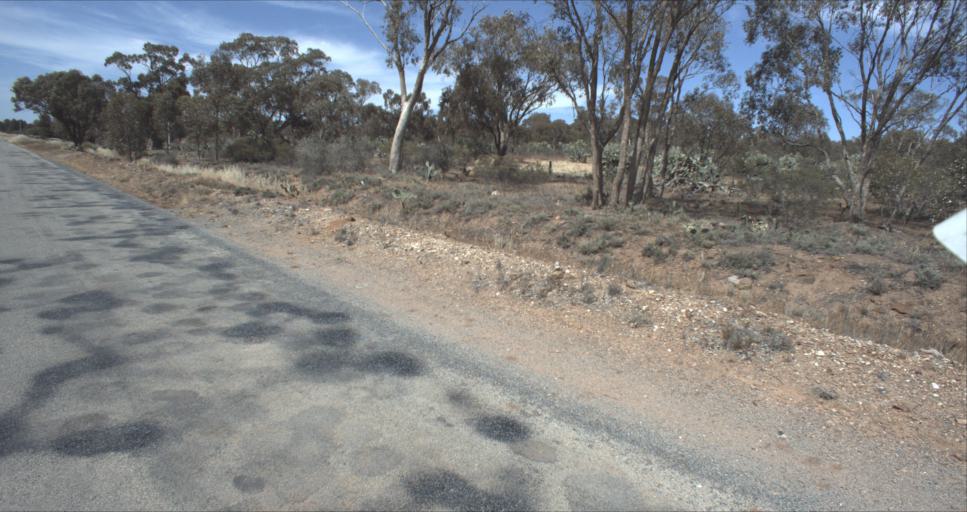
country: AU
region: New South Wales
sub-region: Leeton
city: Leeton
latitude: -34.5635
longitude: 146.4615
